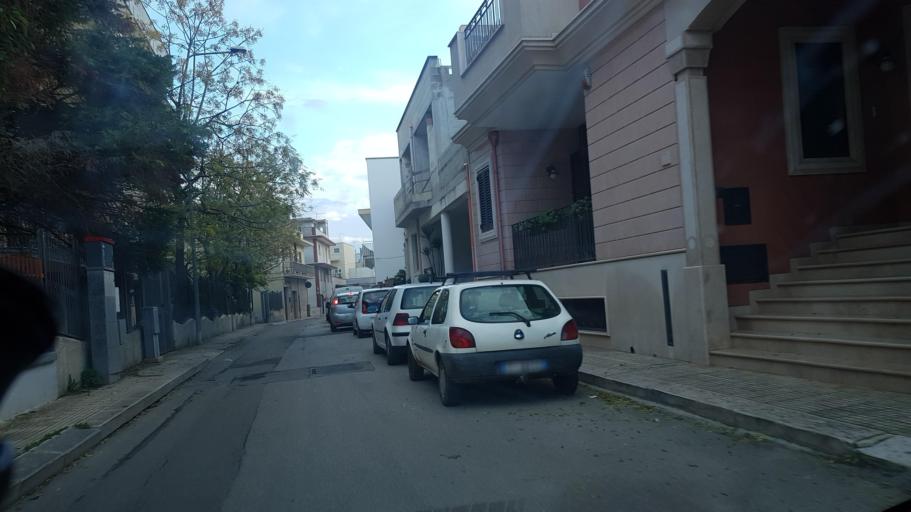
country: IT
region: Apulia
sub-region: Provincia di Brindisi
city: San Vito dei Normanni
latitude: 40.6574
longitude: 17.6979
